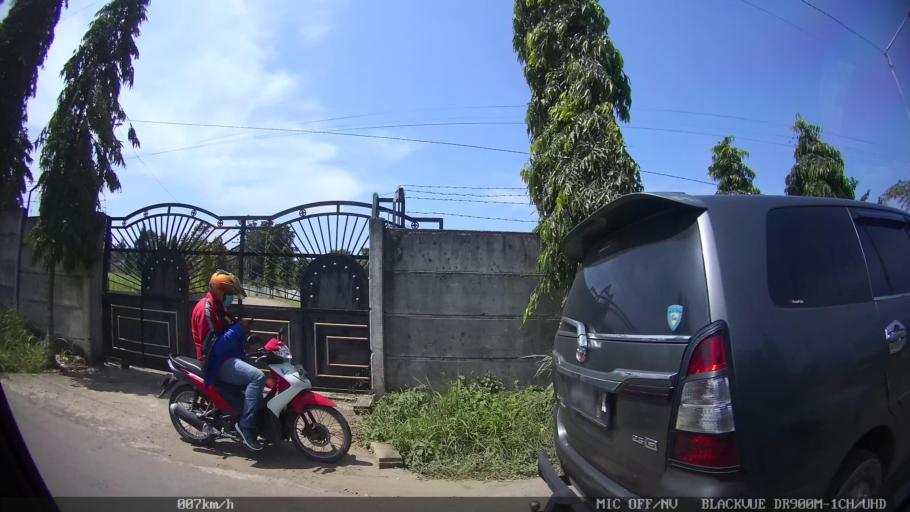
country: ID
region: Lampung
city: Kedaton
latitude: -5.3700
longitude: 105.2587
